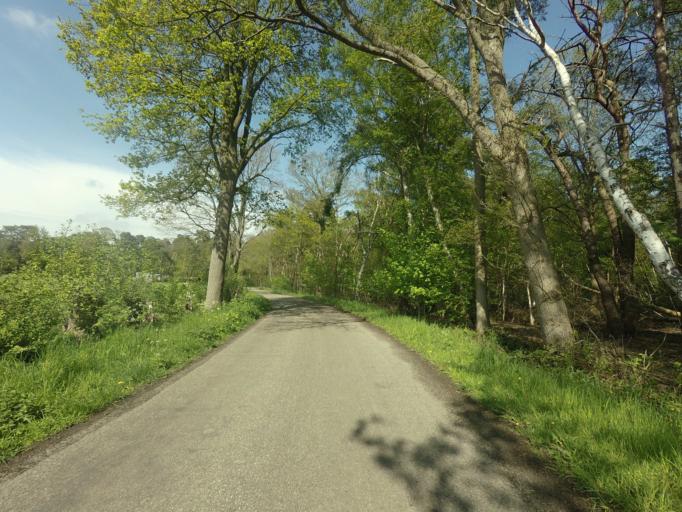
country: NL
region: Overijssel
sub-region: Gemeente Haaksbergen
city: Haaksbergen
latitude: 52.1679
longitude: 6.8033
